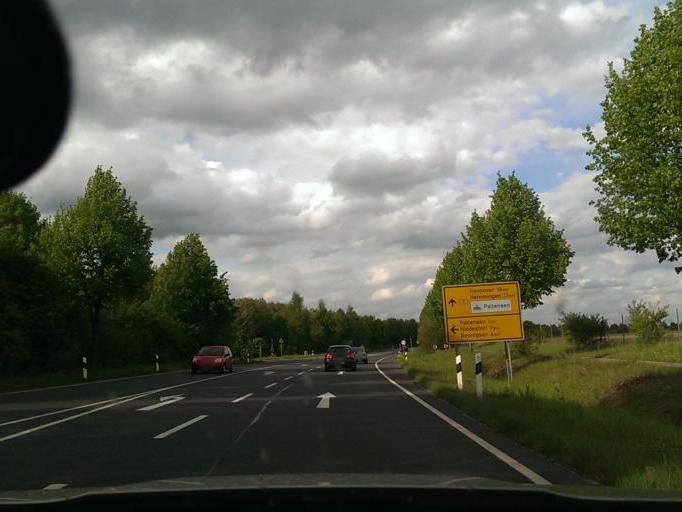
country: DE
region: Lower Saxony
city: Pattensen
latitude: 52.2420
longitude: 9.7571
